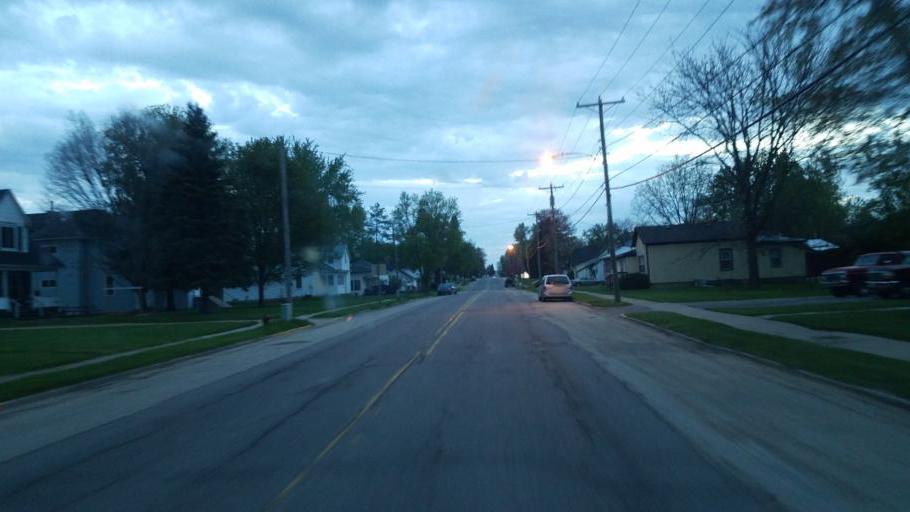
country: US
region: Wisconsin
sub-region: Juneau County
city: Elroy
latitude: 43.7463
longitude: -90.2732
